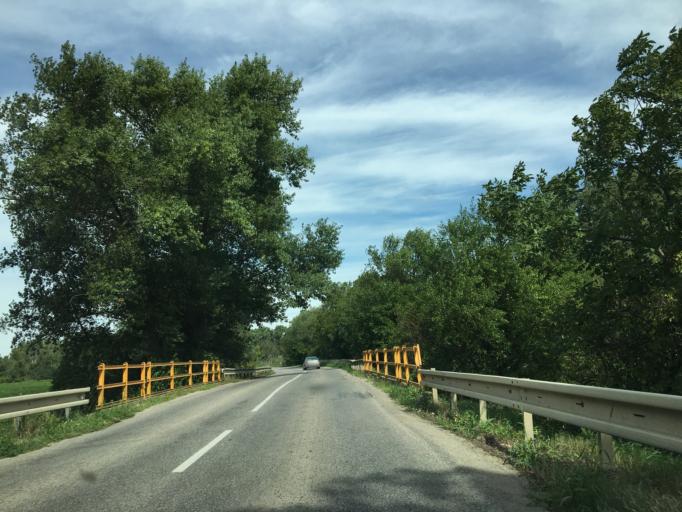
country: SK
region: Nitriansky
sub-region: Okres Nove Zamky
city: Sturovo
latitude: 47.8123
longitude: 18.7222
